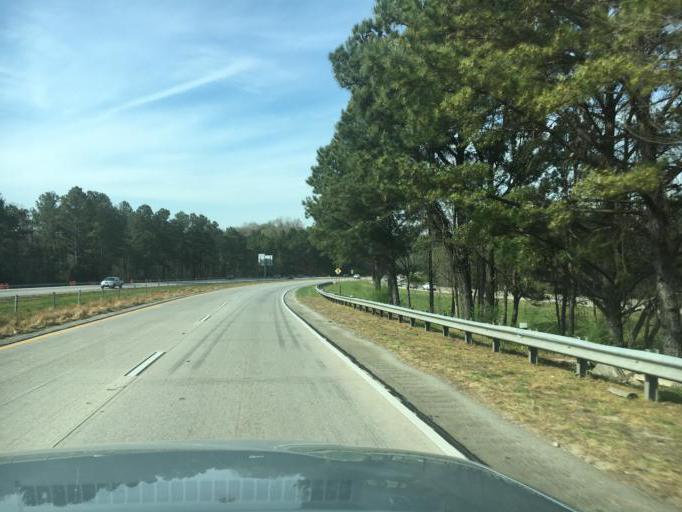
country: US
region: Georgia
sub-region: Hall County
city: Gainesville
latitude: 34.3178
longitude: -83.7887
